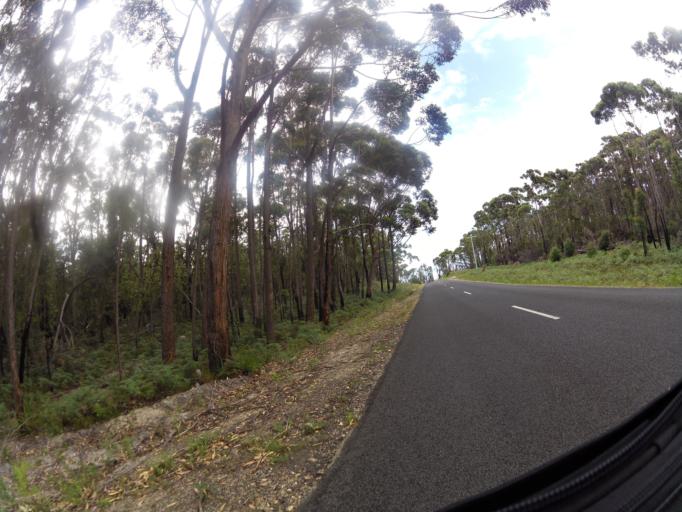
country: AU
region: Victoria
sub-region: East Gippsland
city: Lakes Entrance
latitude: -37.7815
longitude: 148.7303
